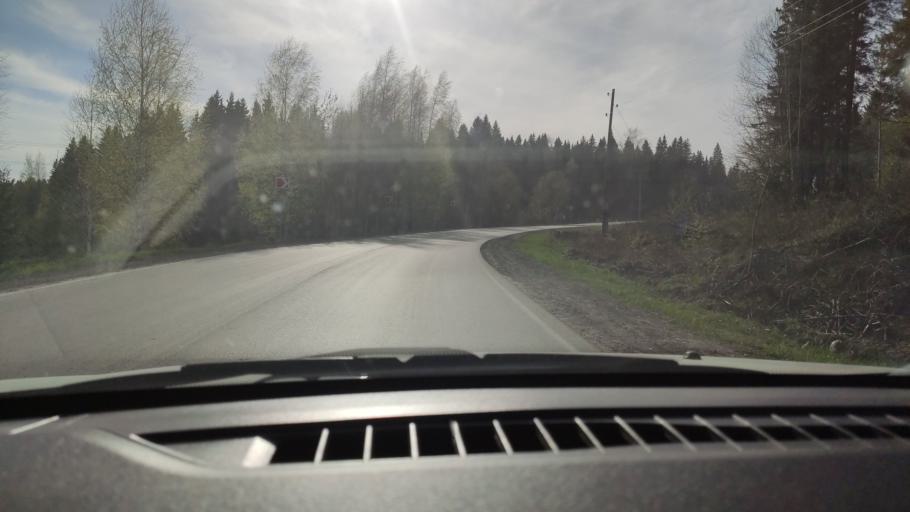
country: RU
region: Perm
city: Novyye Lyady
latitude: 57.9212
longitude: 56.6605
